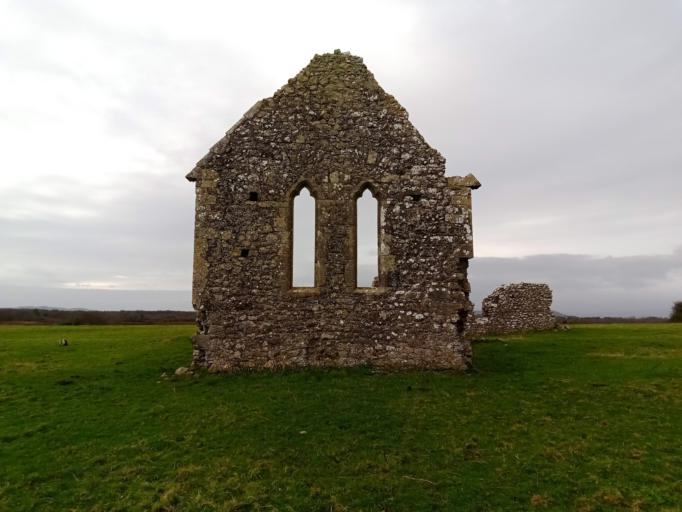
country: IE
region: Munster
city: Thurles
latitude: 52.5974
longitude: -7.7336
